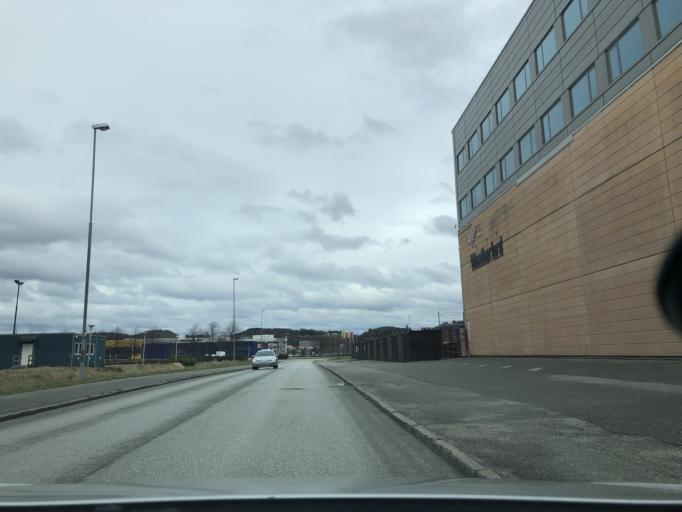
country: NO
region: Rogaland
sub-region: Sandnes
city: Sandnes
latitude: 58.8838
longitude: 5.7219
